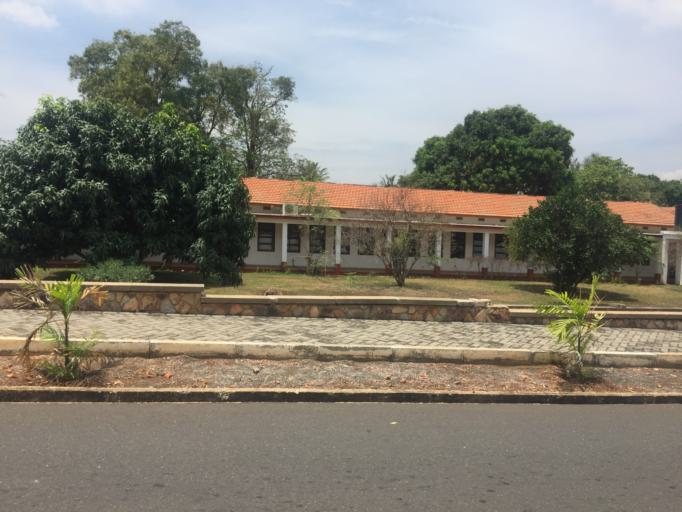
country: GH
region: Greater Accra
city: Medina Estates
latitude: 5.6532
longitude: -0.1879
